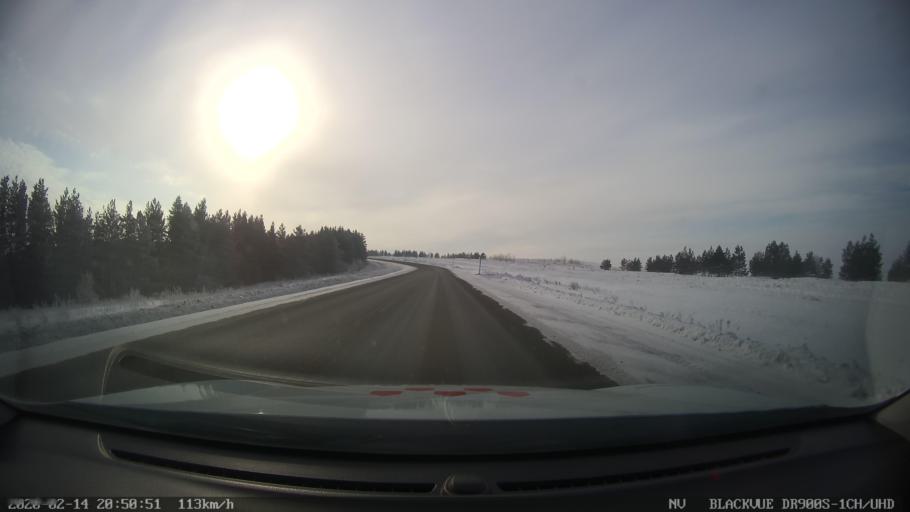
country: RU
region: Tatarstan
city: Kuybyshevskiy Zaton
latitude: 55.2209
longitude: 49.2319
